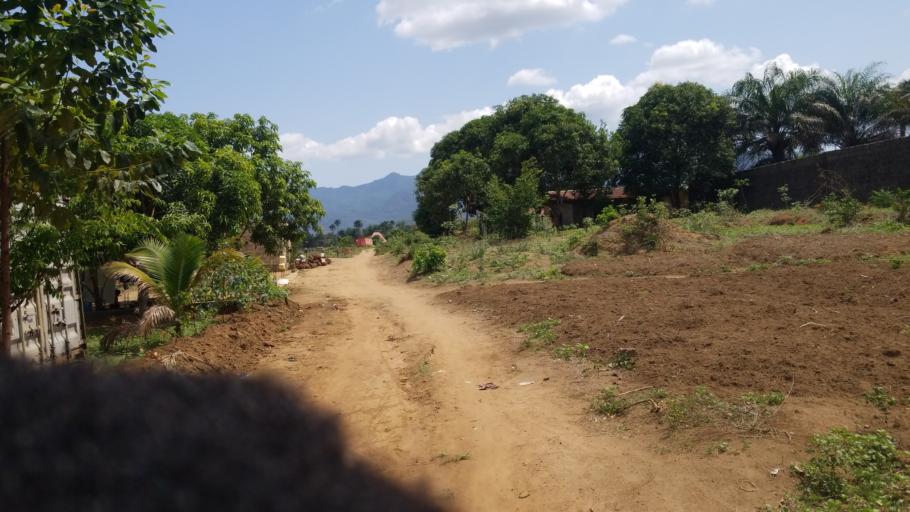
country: SL
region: Western Area
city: Waterloo
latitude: 8.3115
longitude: -13.0559
